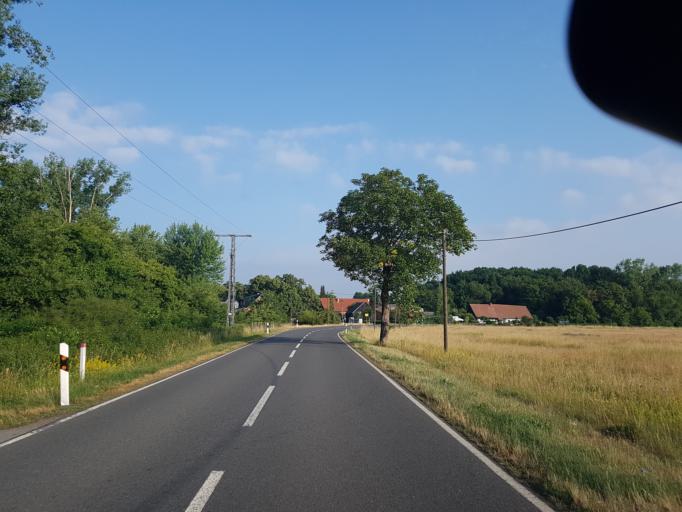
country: DE
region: Saxony-Anhalt
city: Holzdorf
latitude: 51.8264
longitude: 13.1985
